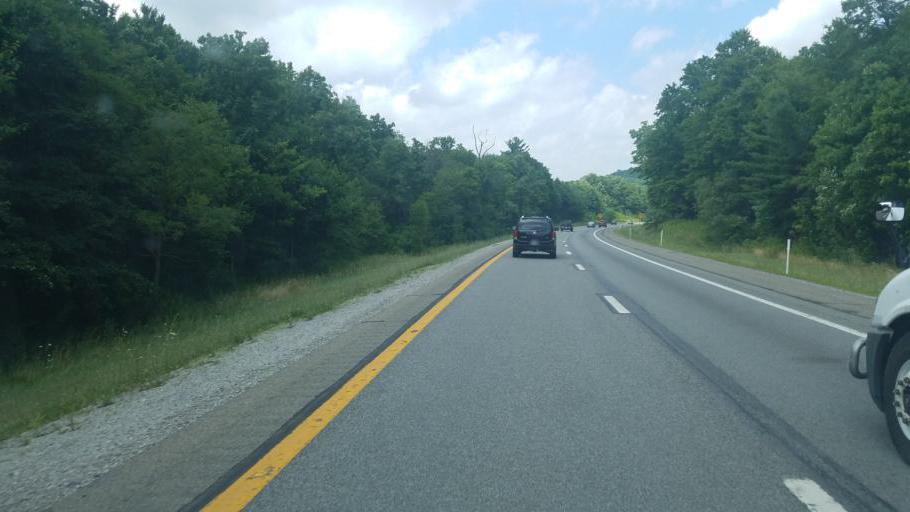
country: US
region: West Virginia
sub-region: Raleigh County
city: Shady Spring
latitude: 37.6870
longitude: -81.1280
